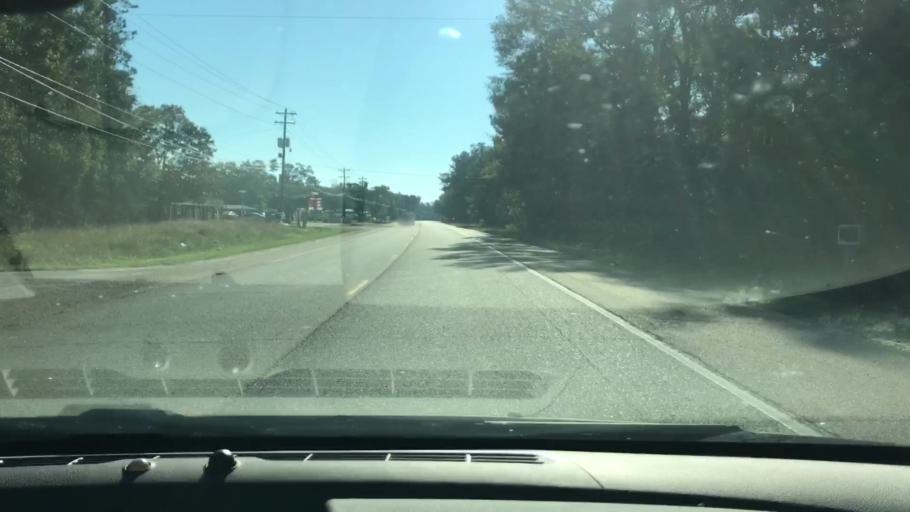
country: US
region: Louisiana
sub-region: Saint Tammany Parish
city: Pearl River
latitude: 30.4124
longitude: -89.7804
